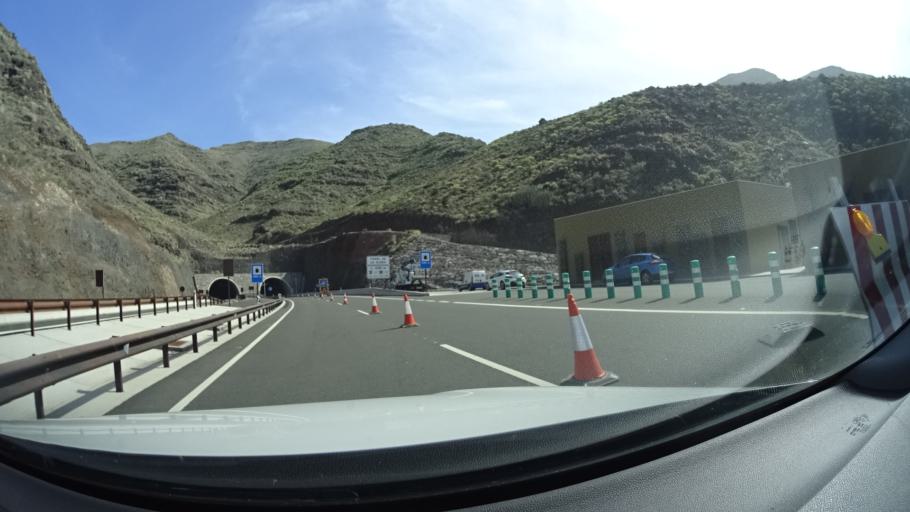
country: ES
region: Canary Islands
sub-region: Provincia de Las Palmas
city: San Nicolas
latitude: 28.0210
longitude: -15.7643
